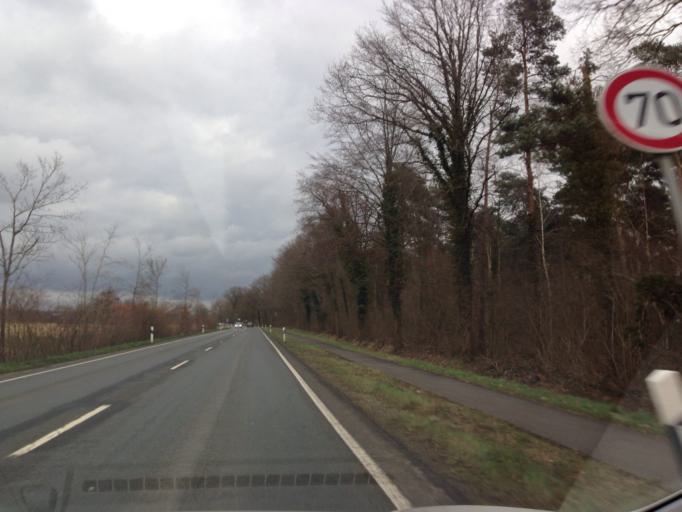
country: DE
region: North Rhine-Westphalia
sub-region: Regierungsbezirk Munster
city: Nordkirchen
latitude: 51.7437
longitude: 7.4871
